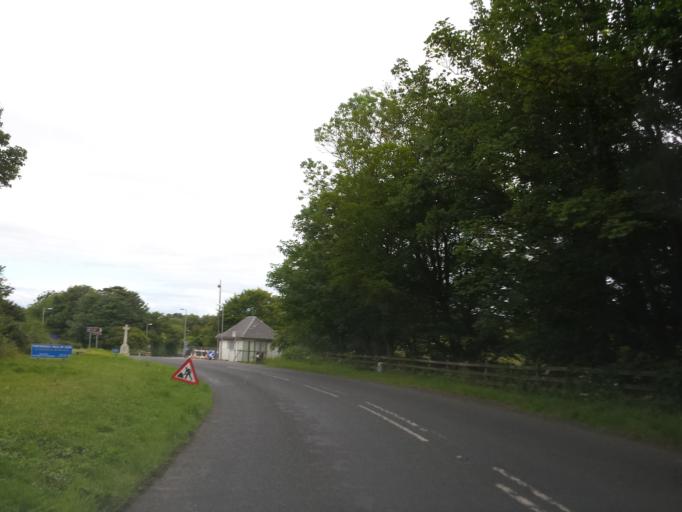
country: GB
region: Scotland
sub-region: Dumfries and Galloway
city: Stranraer
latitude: 54.8489
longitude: -5.1083
